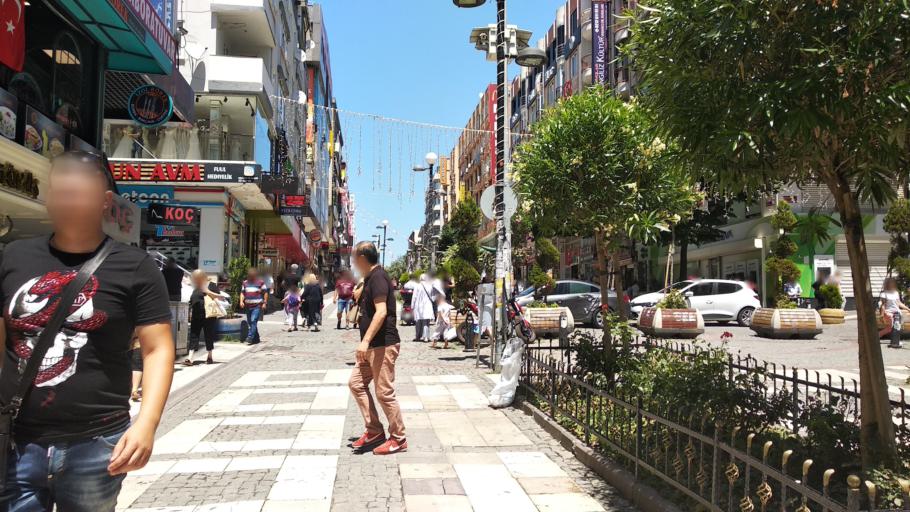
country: TR
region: Istanbul
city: Yakuplu
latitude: 40.9806
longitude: 28.7220
